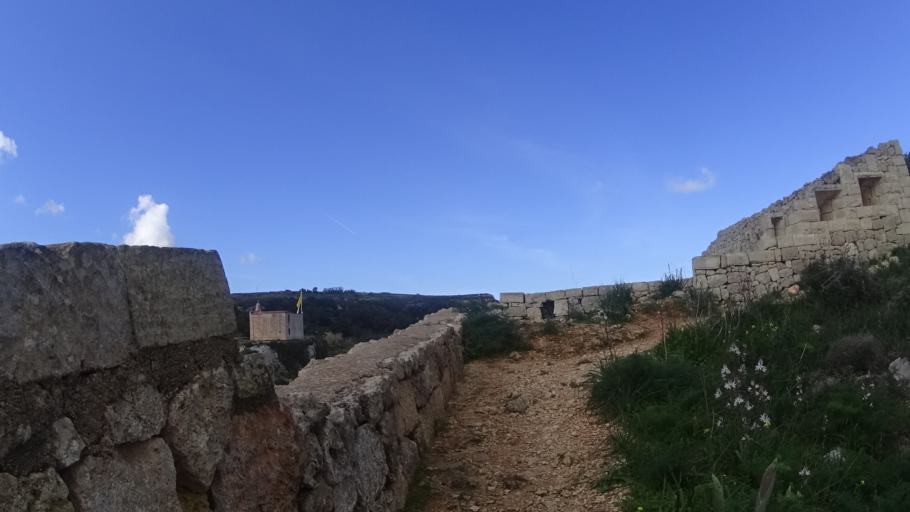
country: MT
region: L-Imgarr
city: Imgarr
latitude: 35.9038
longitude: 14.3786
